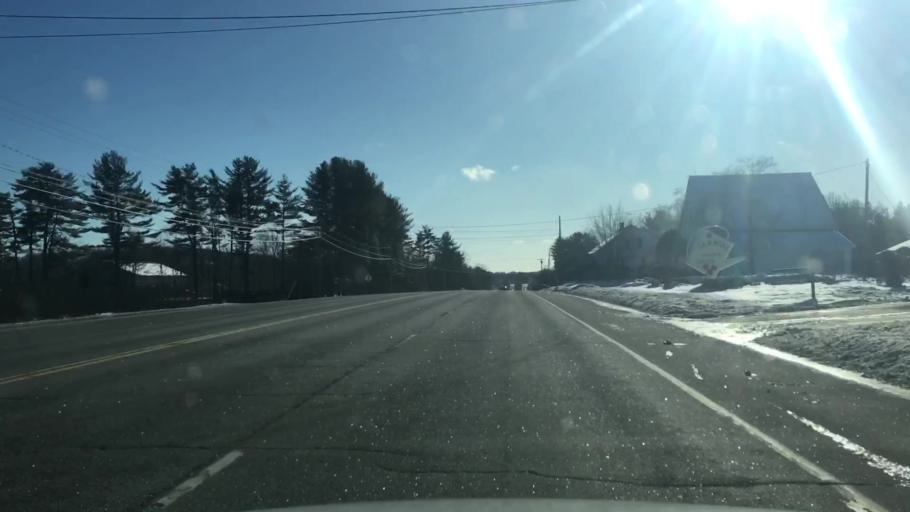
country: US
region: Maine
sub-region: Androscoggin County
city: Lewiston
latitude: 44.1711
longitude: -70.2325
